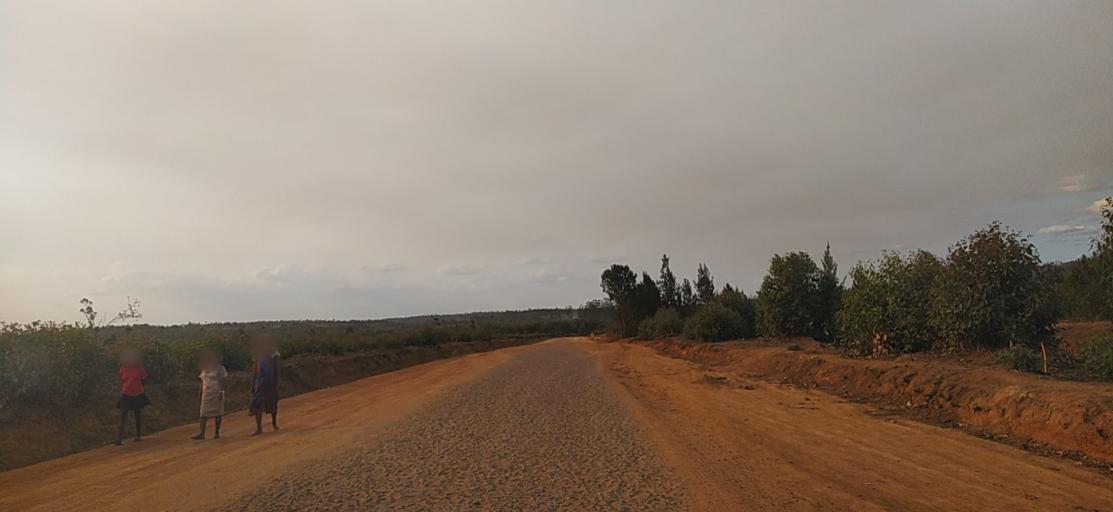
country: MG
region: Alaotra Mangoro
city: Moramanga
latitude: -18.5987
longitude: 48.2783
